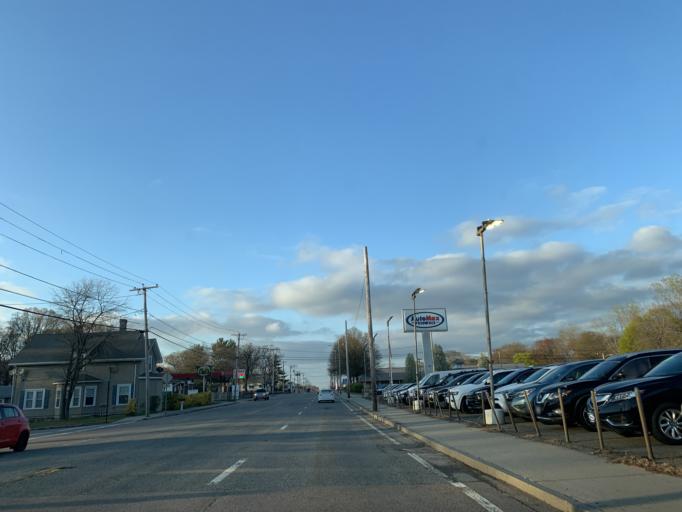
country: US
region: Rhode Island
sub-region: Providence County
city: Valley Falls
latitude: 41.9056
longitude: -71.3655
